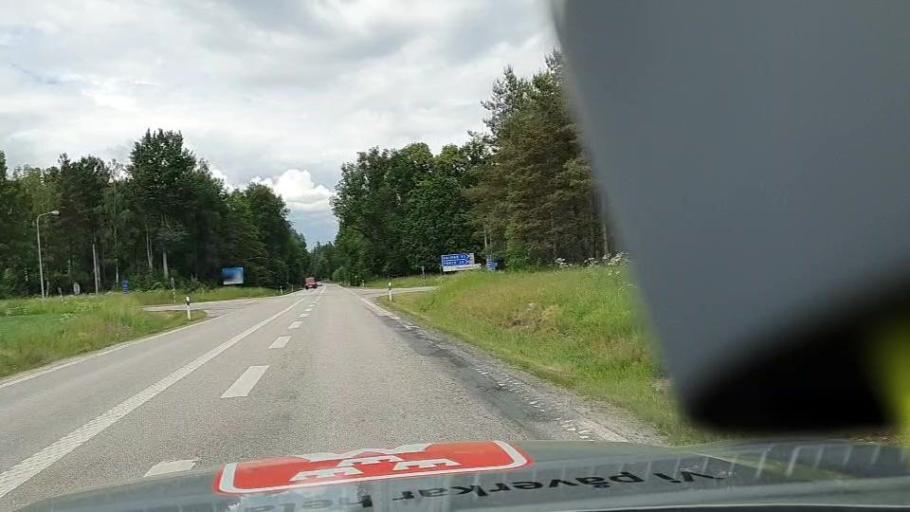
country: SE
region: Kalmar
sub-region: Emmaboda Kommun
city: Emmaboda
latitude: 56.5337
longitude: 15.6124
